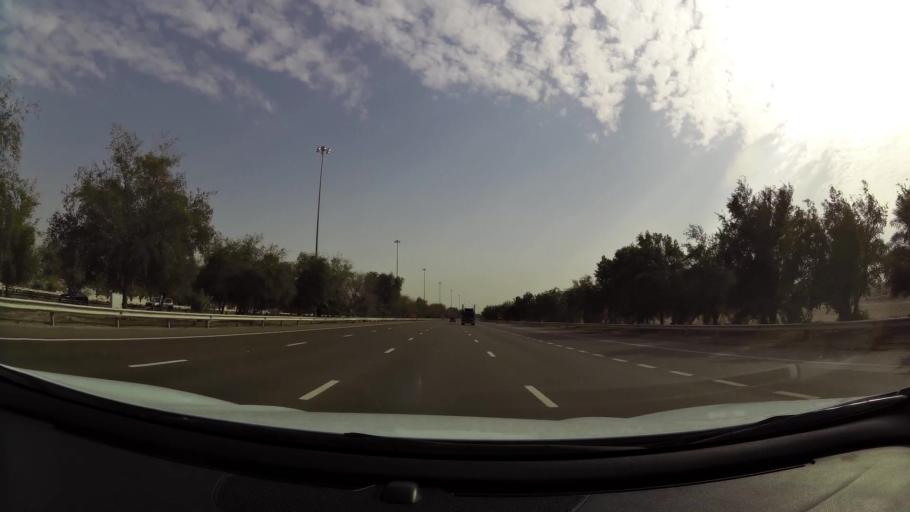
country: AE
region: Abu Dhabi
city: Abu Dhabi
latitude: 24.4521
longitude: 54.6785
